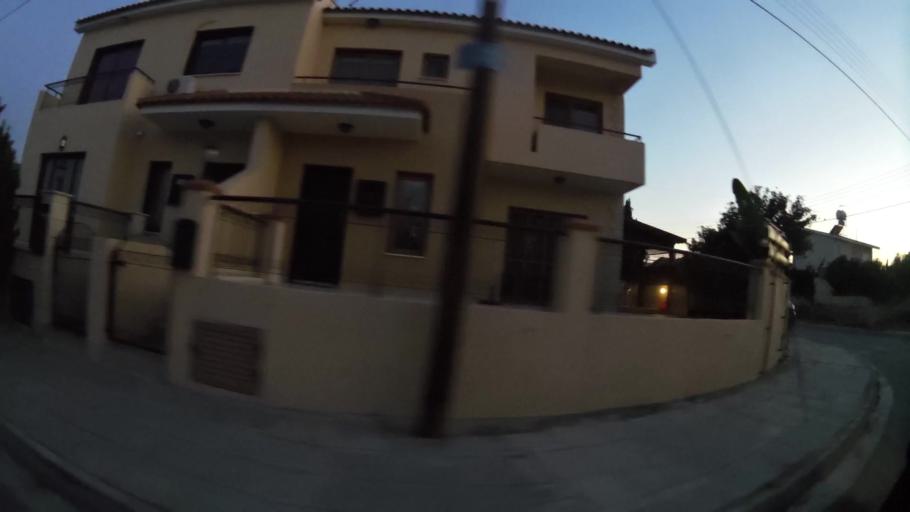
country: CY
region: Larnaka
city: Larnaca
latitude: 34.9134
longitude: 33.5881
